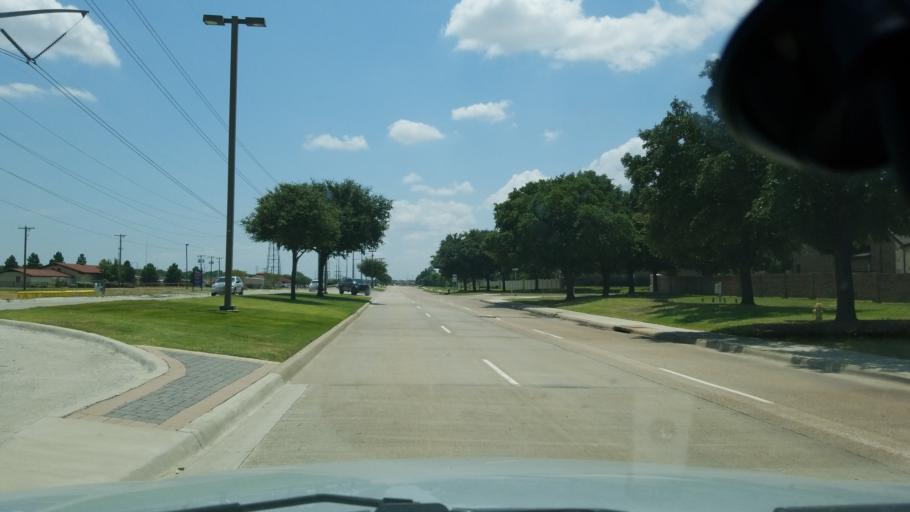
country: US
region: Texas
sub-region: Dallas County
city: Farmers Branch
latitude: 32.8934
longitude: -96.9372
